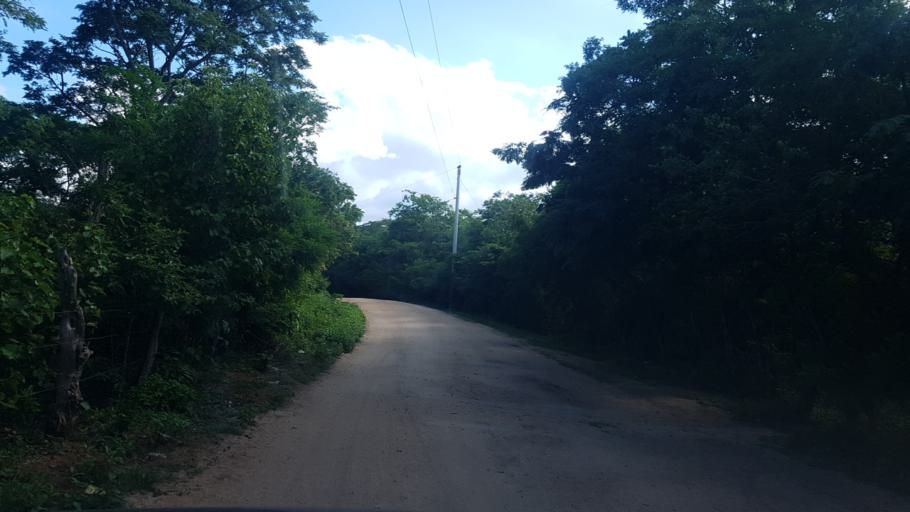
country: NI
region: Nueva Segovia
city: Mozonte
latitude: 13.6532
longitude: -86.3982
